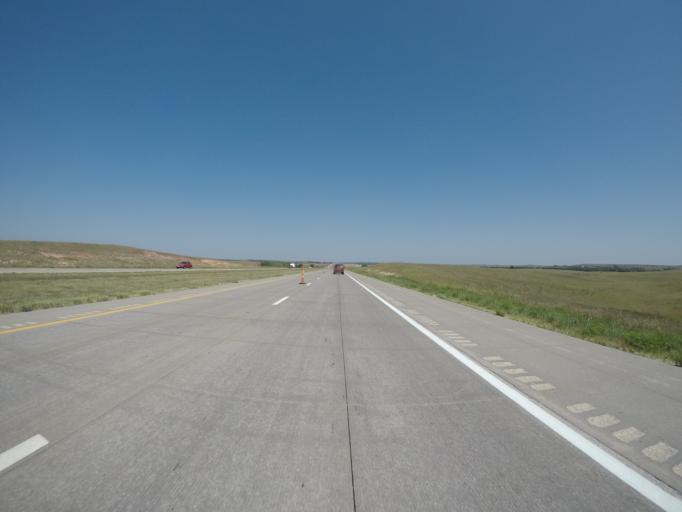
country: US
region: Kansas
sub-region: Lincoln County
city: Lincoln
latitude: 38.8782
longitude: -98.0059
